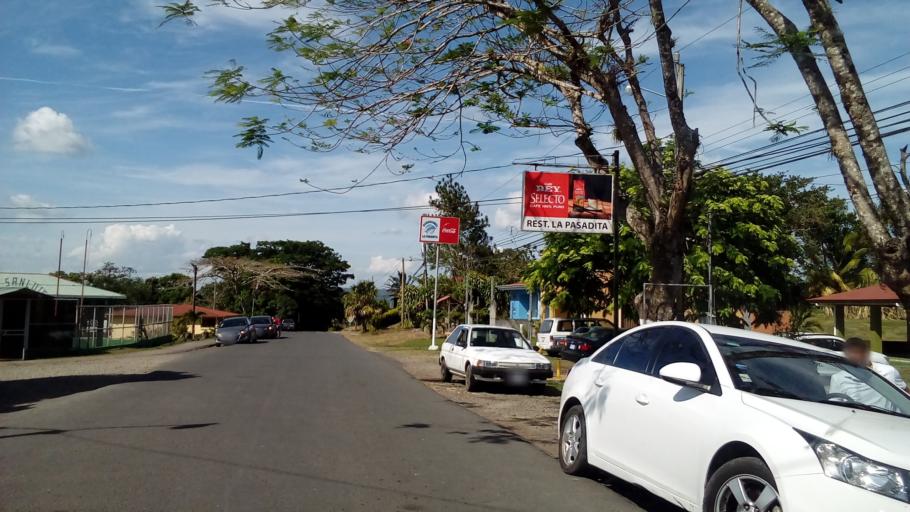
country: CR
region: Guanacaste
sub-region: Canton de Tilaran
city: Tilaran
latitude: 10.5026
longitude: -84.9426
